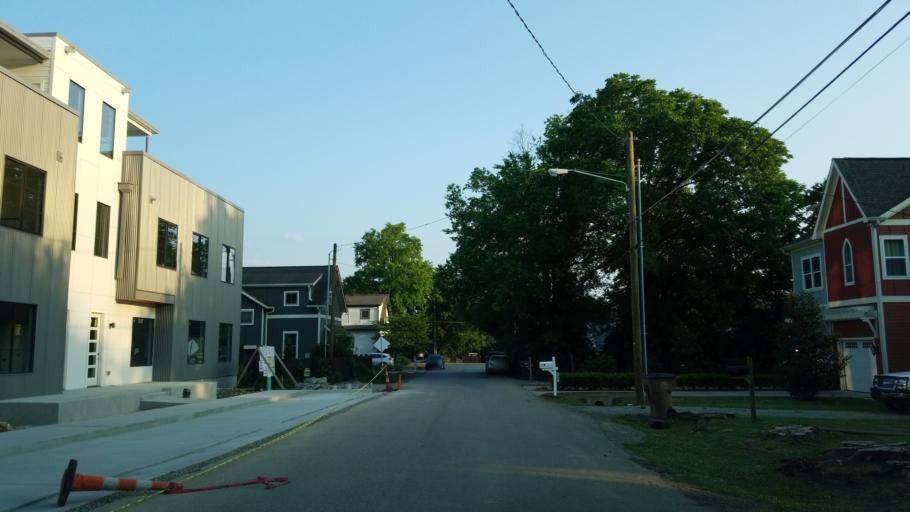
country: US
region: Tennessee
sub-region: Davidson County
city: Nashville
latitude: 36.1393
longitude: -86.7667
